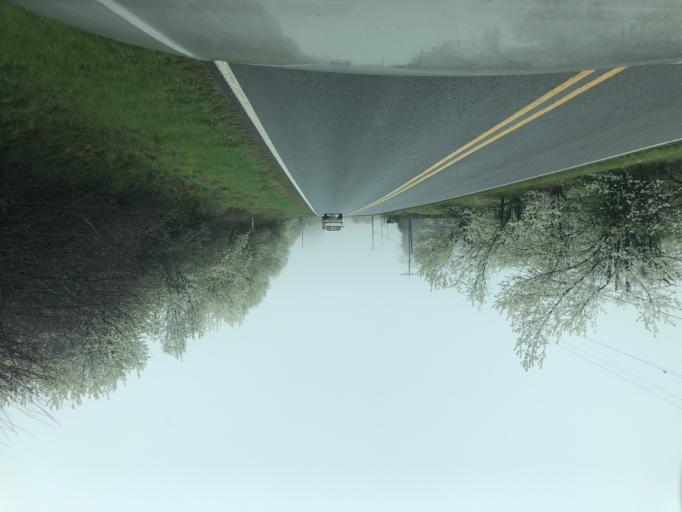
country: US
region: North Carolina
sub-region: Cleveland County
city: Shelby
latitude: 35.3191
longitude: -81.4811
